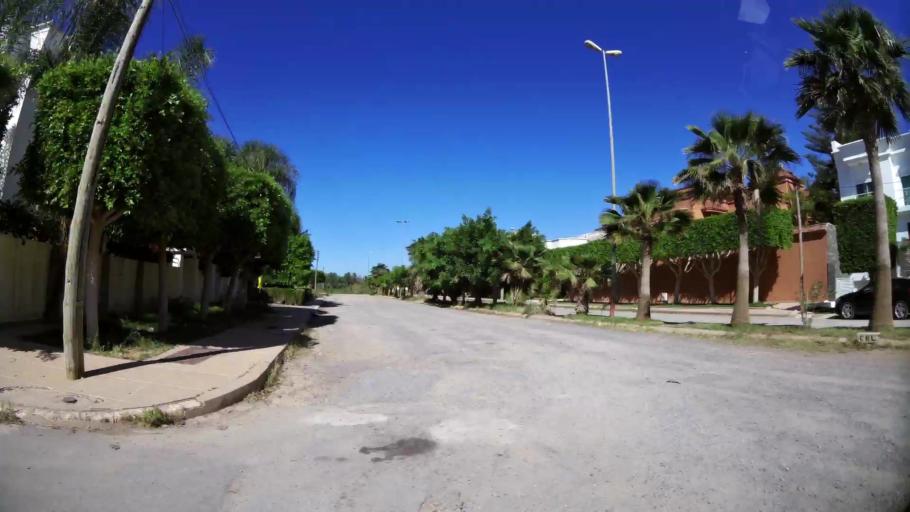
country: MA
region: Oriental
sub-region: Berkane-Taourirt
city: Berkane
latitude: 34.9438
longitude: -2.3341
